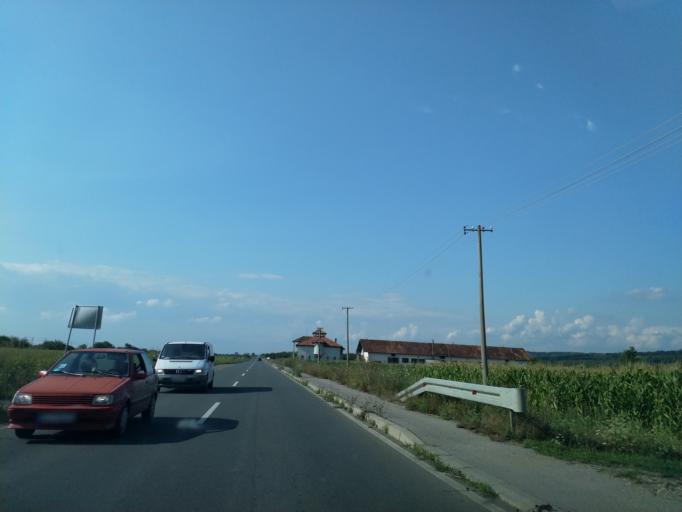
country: RS
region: Central Serbia
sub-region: Pomoravski Okrug
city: Paracin
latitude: 43.8065
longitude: 21.4211
